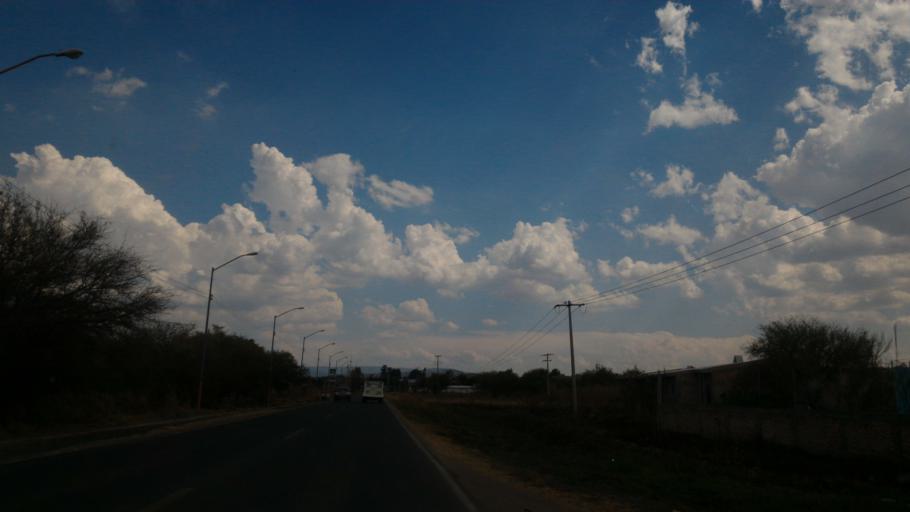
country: MX
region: Guanajuato
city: Ciudad Manuel Doblado
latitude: 20.7415
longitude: -101.9562
